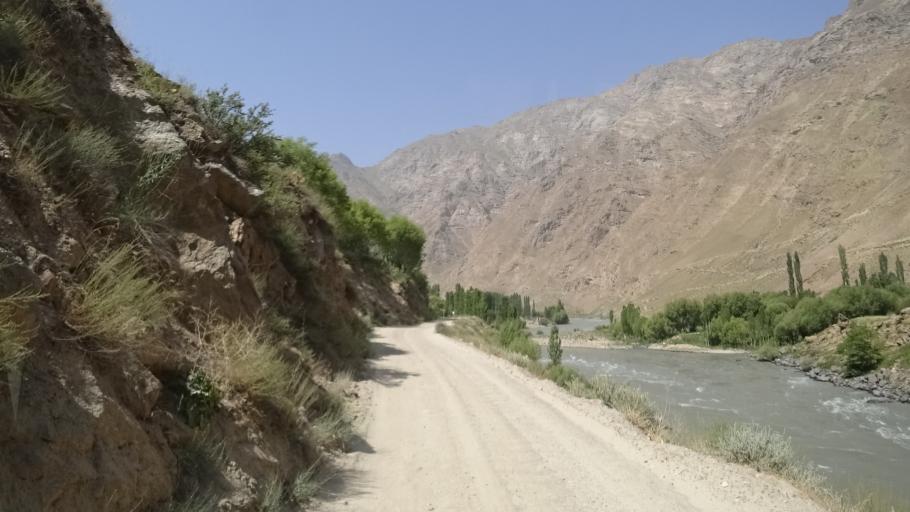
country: TJ
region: Gorno-Badakhshan
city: Khorugh
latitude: 37.1831
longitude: 71.4598
